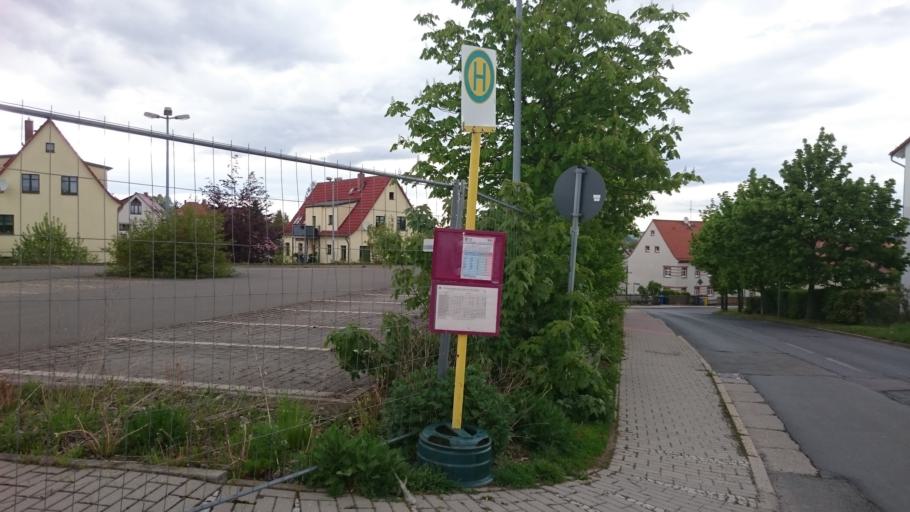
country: DE
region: Saxony
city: Wilkau-Hasslau
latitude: 50.6690
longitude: 12.5032
